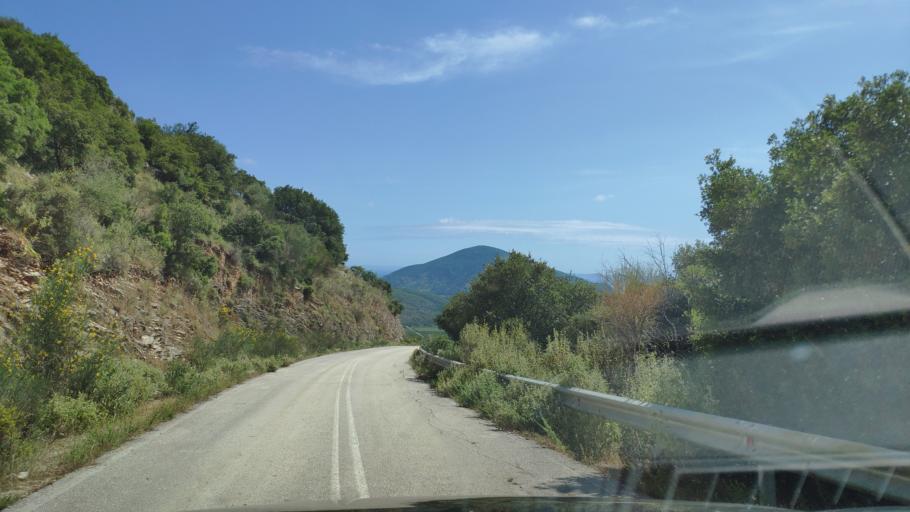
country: AL
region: Vlore
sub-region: Rrethi i Sarandes
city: Konispol
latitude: 39.6351
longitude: 20.2059
